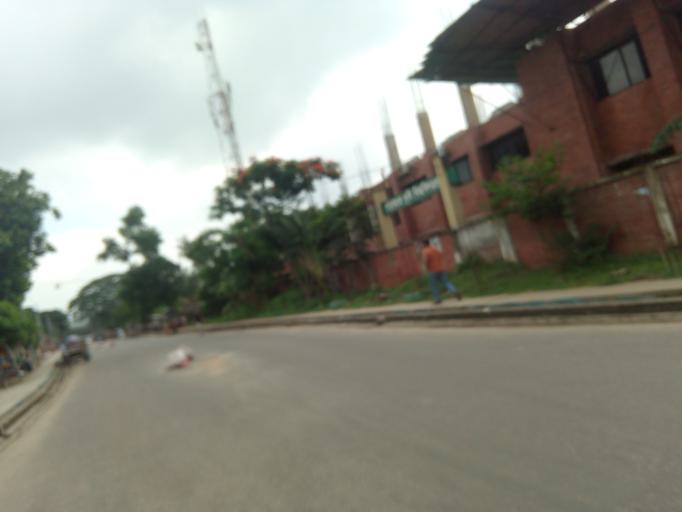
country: BD
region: Dhaka
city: Azimpur
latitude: 23.7701
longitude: 90.3726
